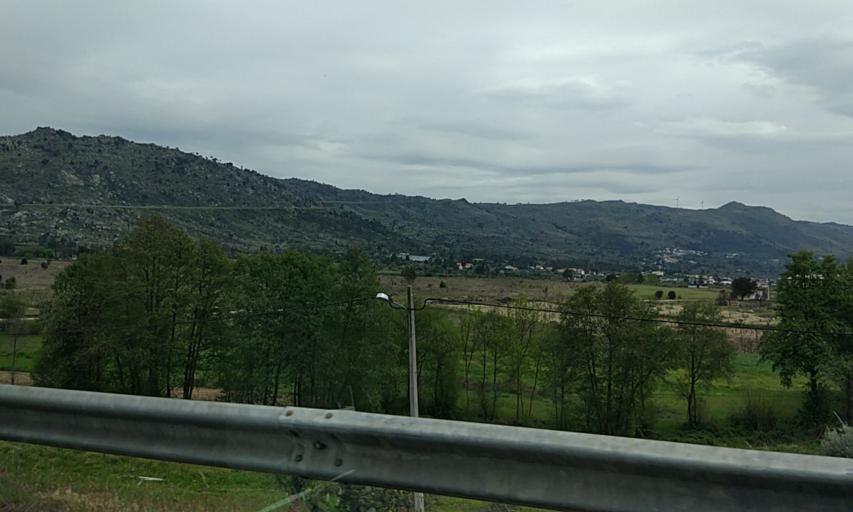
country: PT
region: Guarda
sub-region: Guarda
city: Guarda
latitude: 40.6220
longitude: -7.2993
